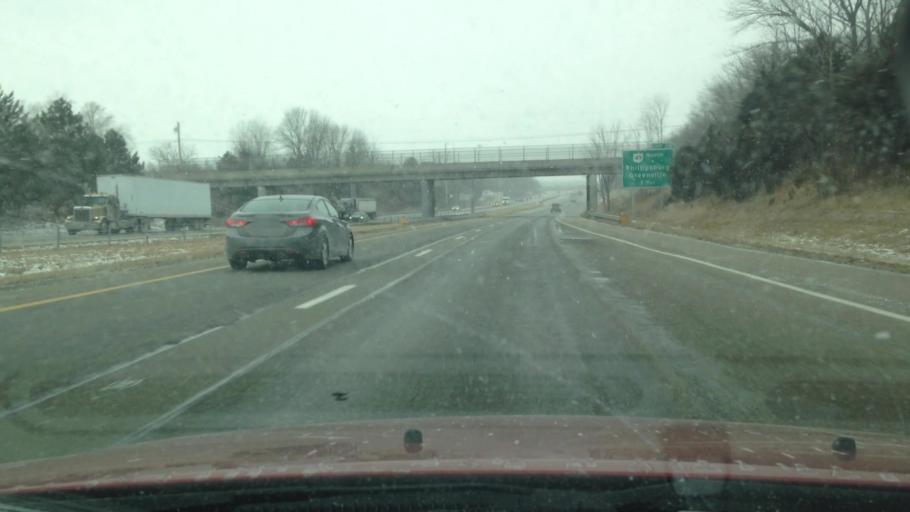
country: US
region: Ohio
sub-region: Montgomery County
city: Clayton
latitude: 39.8542
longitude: -84.3479
